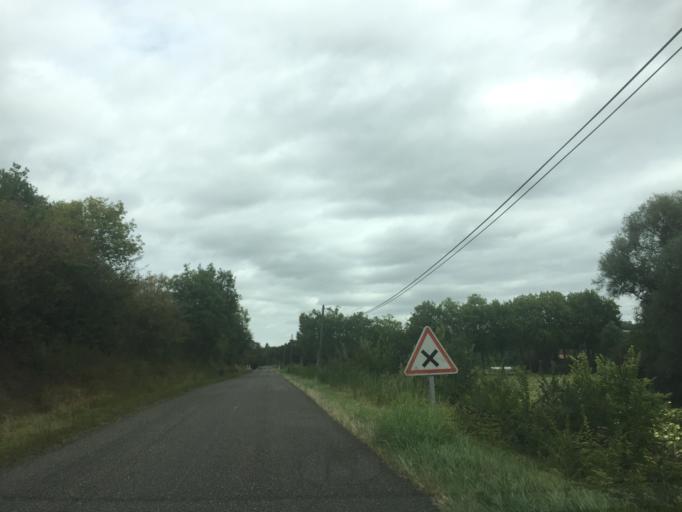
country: FR
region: Midi-Pyrenees
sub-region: Departement du Gers
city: Mirande
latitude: 43.6259
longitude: 0.3498
